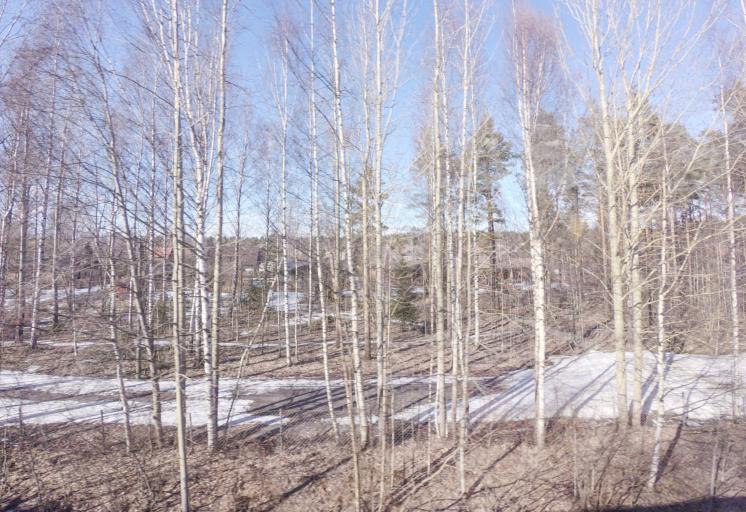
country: FI
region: South Karelia
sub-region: Lappeenranta
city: Lappeenranta
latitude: 61.0537
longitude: 28.2138
